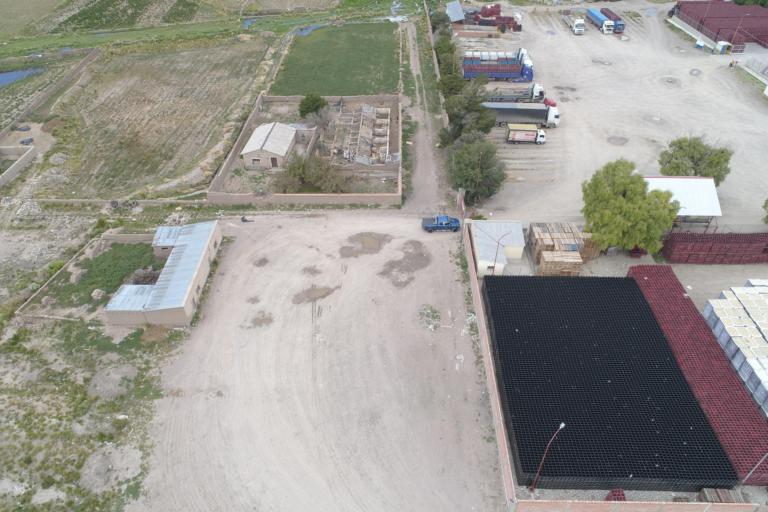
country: BO
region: Oruro
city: Challapata
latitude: -19.0123
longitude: -66.7825
